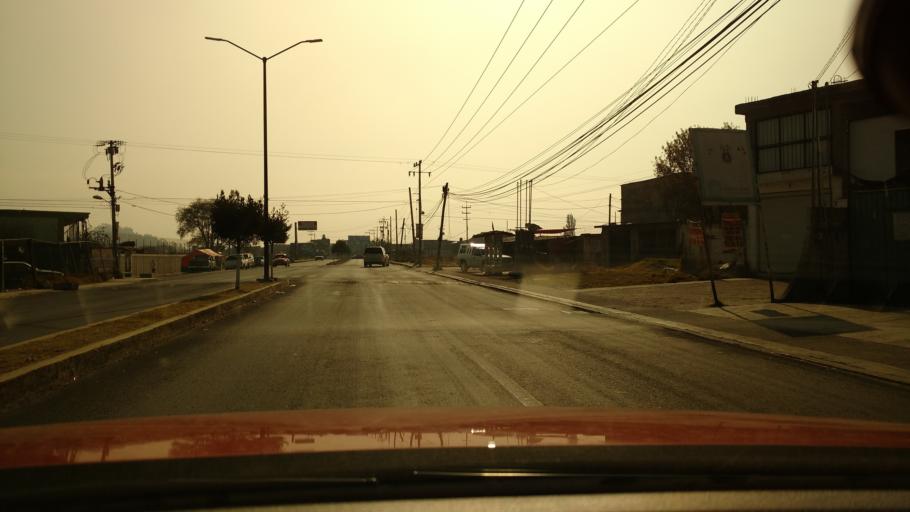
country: MX
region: Mexico
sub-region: Calimaya
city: Colonia Arboledas (San Andres)
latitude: 19.2066
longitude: -99.5785
